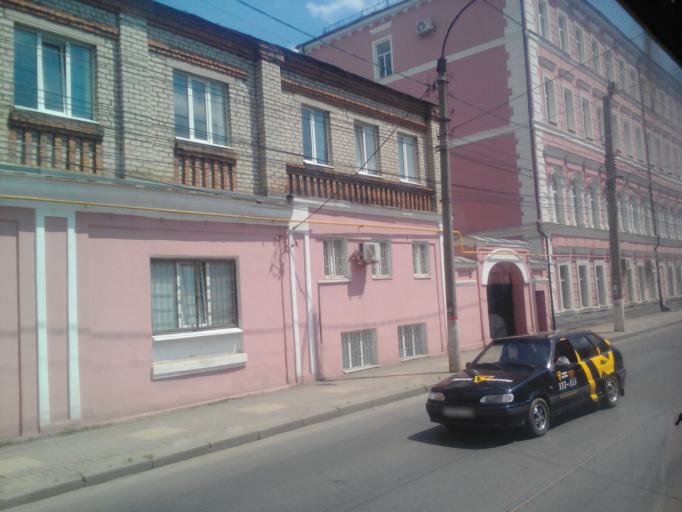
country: RU
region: Kursk
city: Kursk
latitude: 51.7243
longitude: 36.1874
